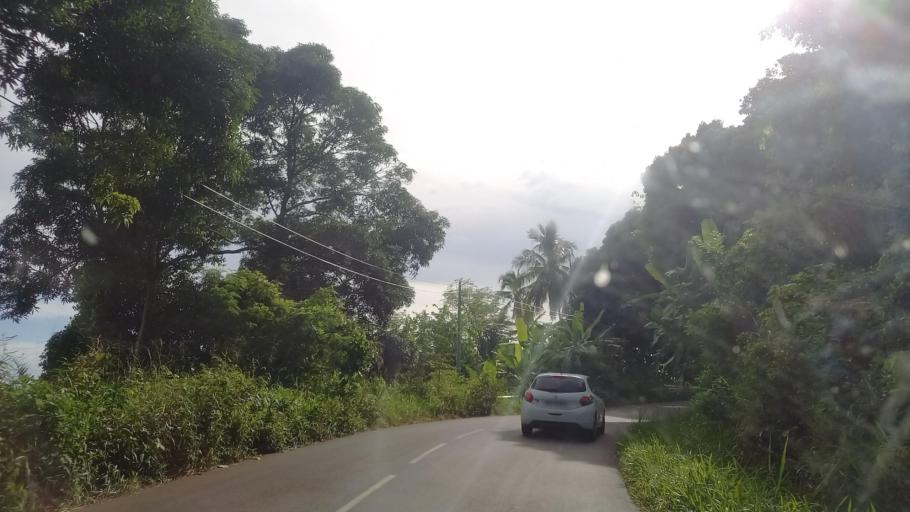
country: YT
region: Sada
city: Sada
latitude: -12.8620
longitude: 45.1079
